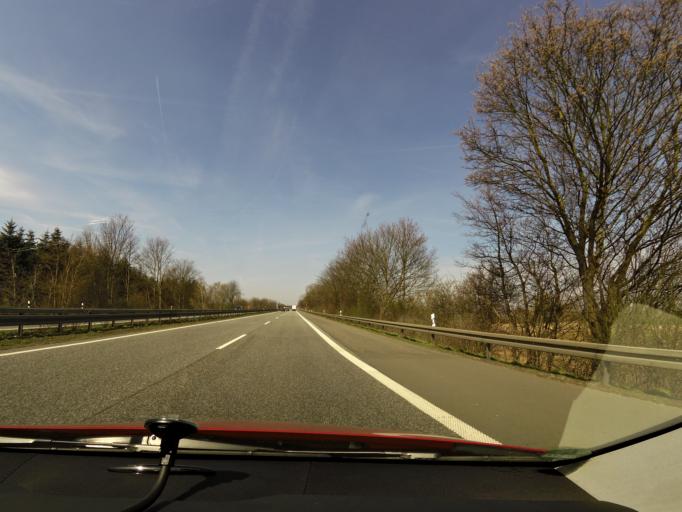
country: DE
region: North Rhine-Westphalia
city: Meckenheim
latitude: 50.5956
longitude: 7.0234
